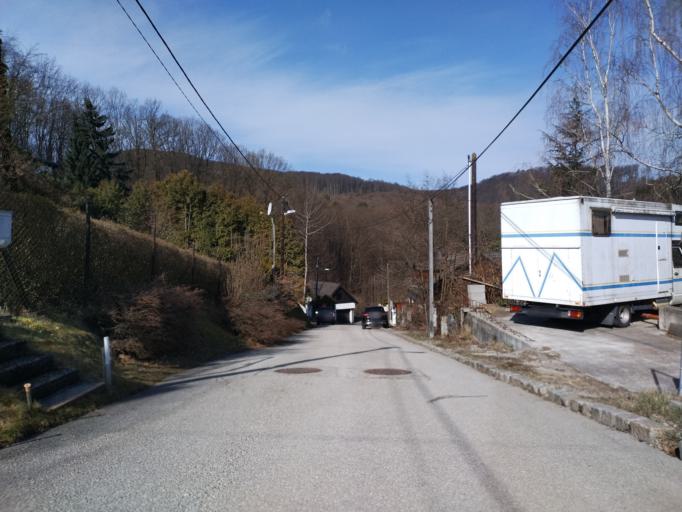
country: AT
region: Lower Austria
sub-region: Politischer Bezirk Wien-Umgebung
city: Gablitz
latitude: 48.2218
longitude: 16.1307
